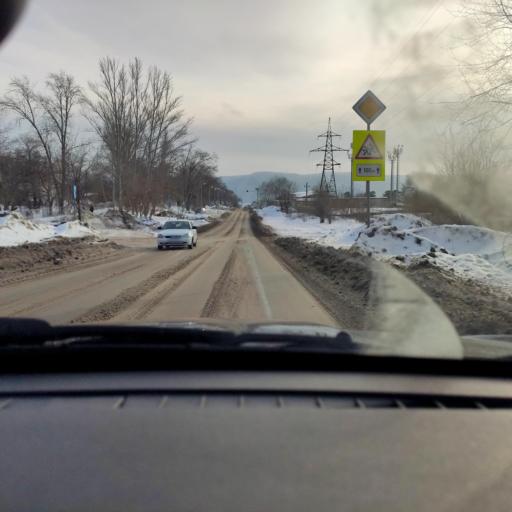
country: RU
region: Samara
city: Pribrezhnyy
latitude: 53.4895
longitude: 49.8470
